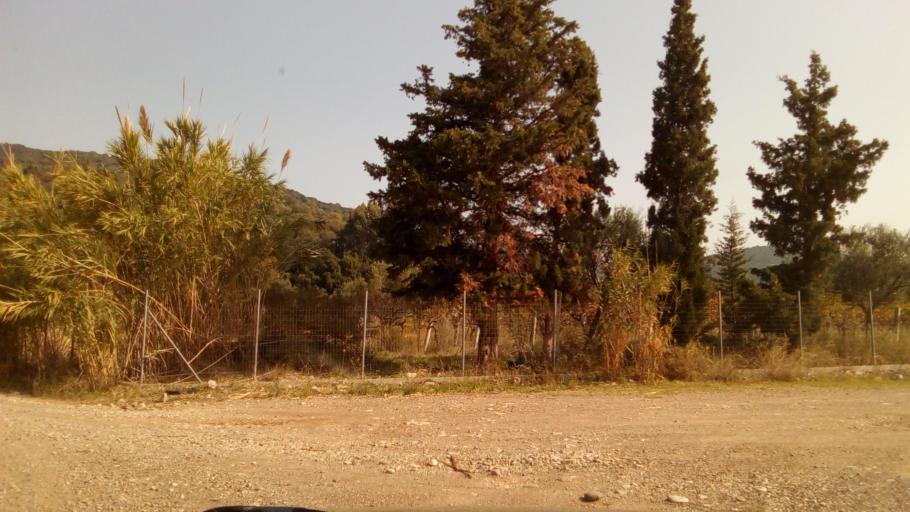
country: GR
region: West Greece
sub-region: Nomos Aitolias kai Akarnanias
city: Nafpaktos
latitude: 38.4169
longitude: 21.8837
